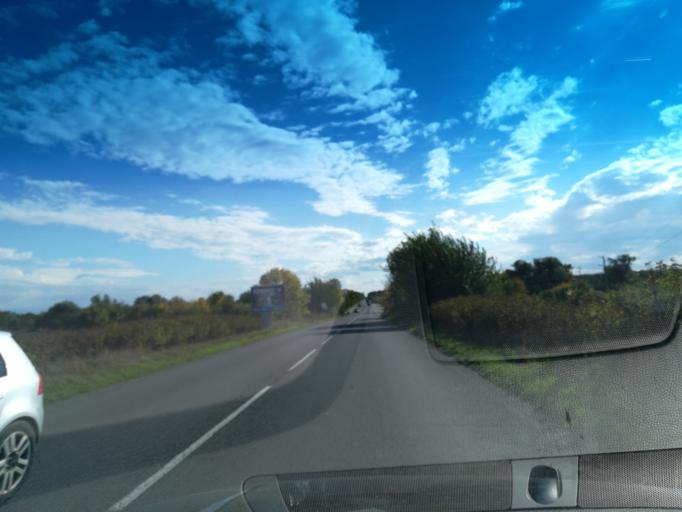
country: BG
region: Stara Zagora
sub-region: Obshtina Stara Zagora
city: Stara Zagora
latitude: 42.3626
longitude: 25.6554
